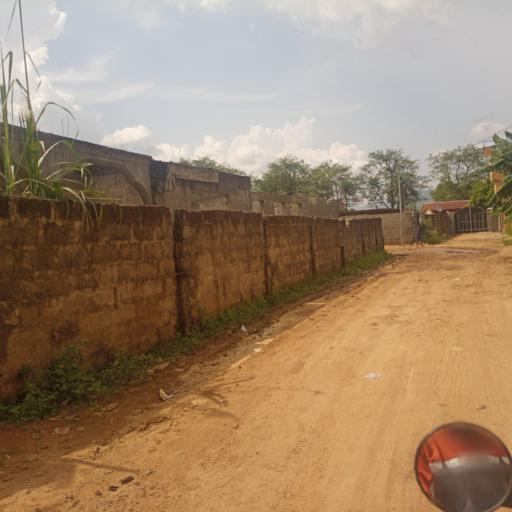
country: SL
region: Western Area
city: Hastings
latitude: 8.3866
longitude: -13.1411
